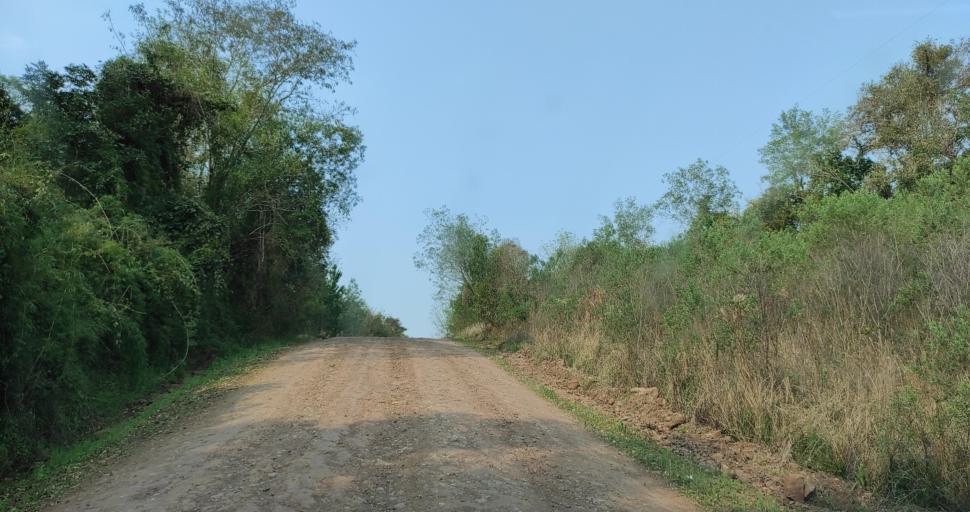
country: AR
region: Misiones
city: Cerro Azul
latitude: -27.6260
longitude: -55.5371
